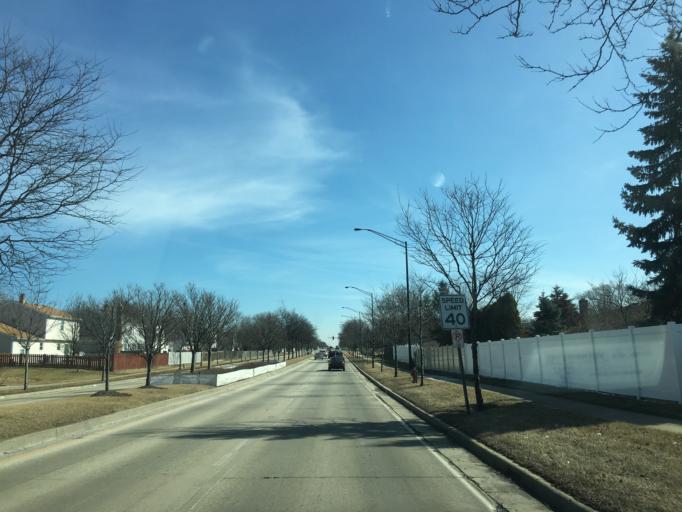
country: US
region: Illinois
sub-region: DuPage County
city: Hanover Park
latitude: 42.0252
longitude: -88.1325
